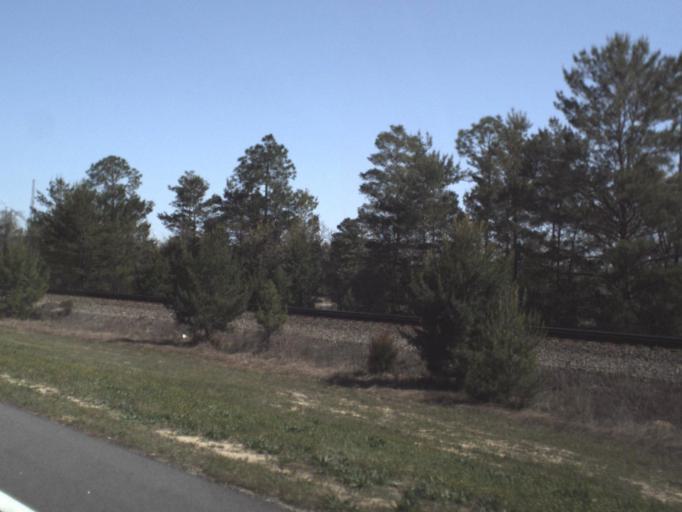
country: US
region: Florida
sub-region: Okaloosa County
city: Crestview
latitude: 30.7357
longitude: -86.3576
